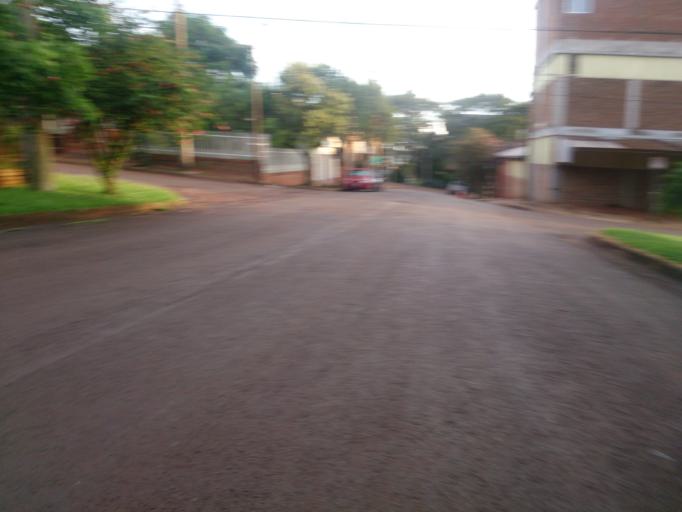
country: AR
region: Misiones
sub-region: Departamento de Obera
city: Obera
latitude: -27.4911
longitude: -55.1065
